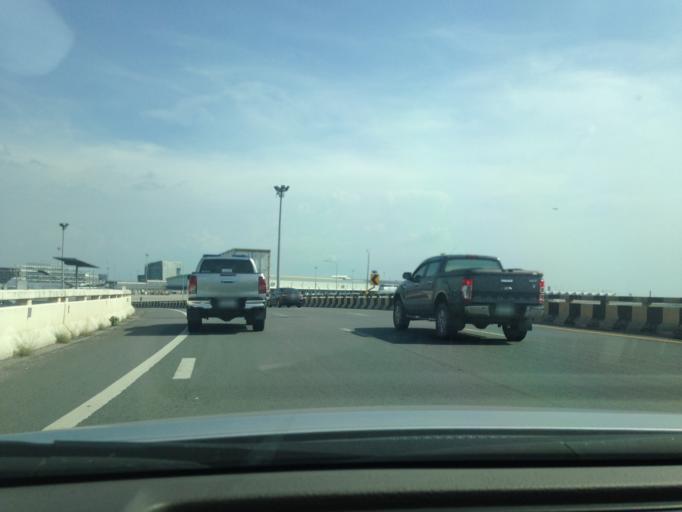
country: TH
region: Bangkok
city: Lat Krabang
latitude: 13.7163
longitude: 100.7468
